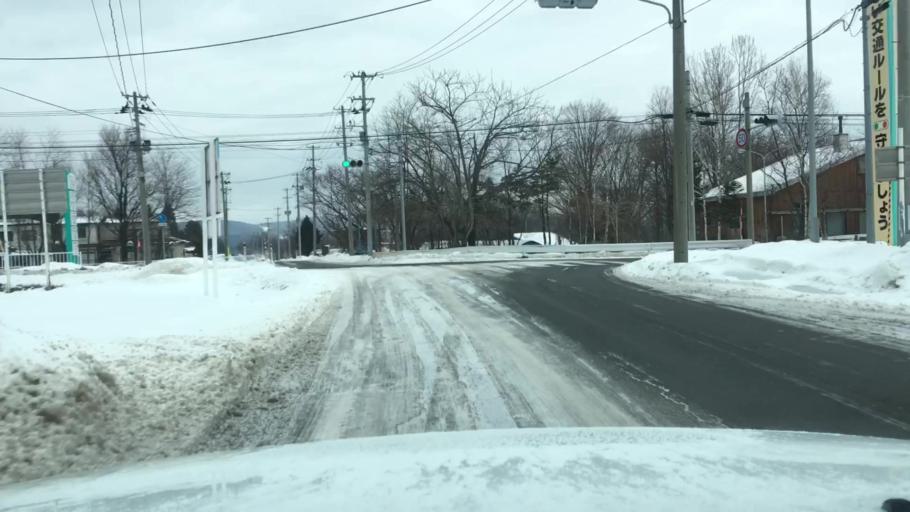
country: JP
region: Iwate
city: Shizukuishi
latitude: 39.9164
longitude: 141.0059
